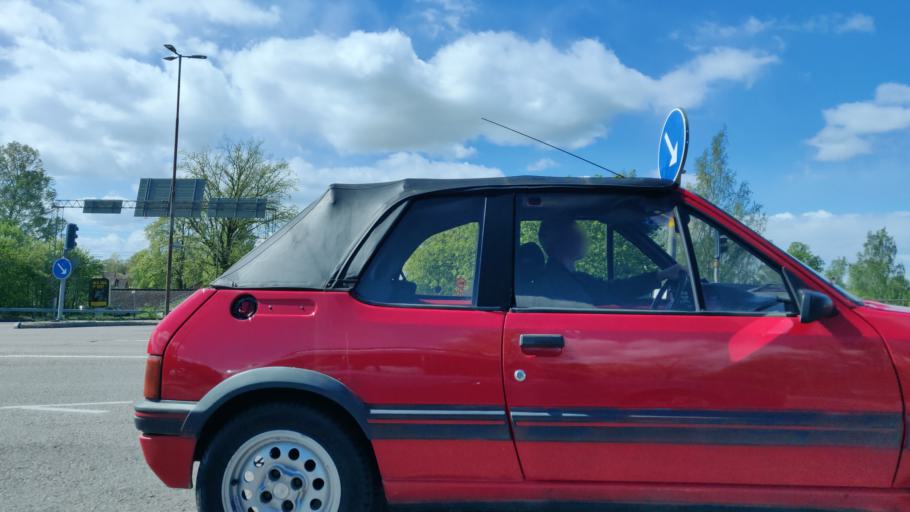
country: SE
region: Vaermland
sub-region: Karlstads Kommun
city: Karlstad
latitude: 59.3801
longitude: 13.4887
